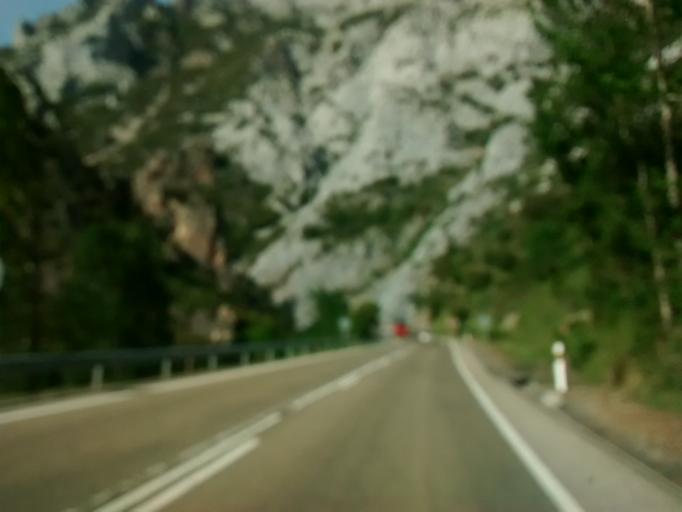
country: ES
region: Cantabria
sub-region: Provincia de Cantabria
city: Potes
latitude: 43.1979
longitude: -4.5922
